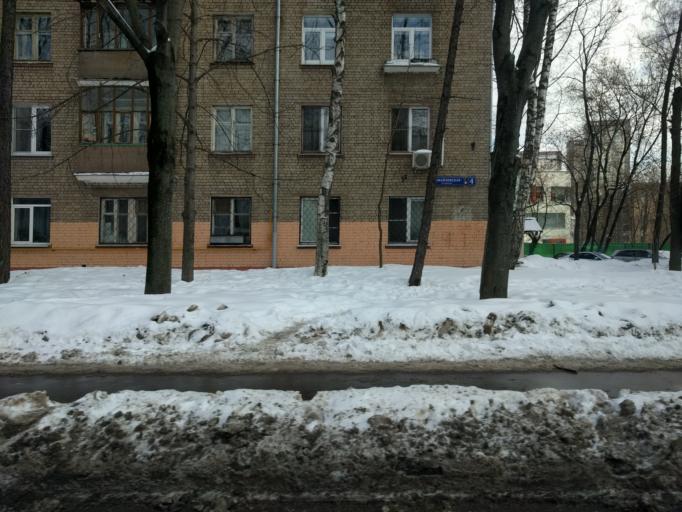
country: RU
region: Moscow
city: Metrogorodok
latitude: 55.7930
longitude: 37.7765
